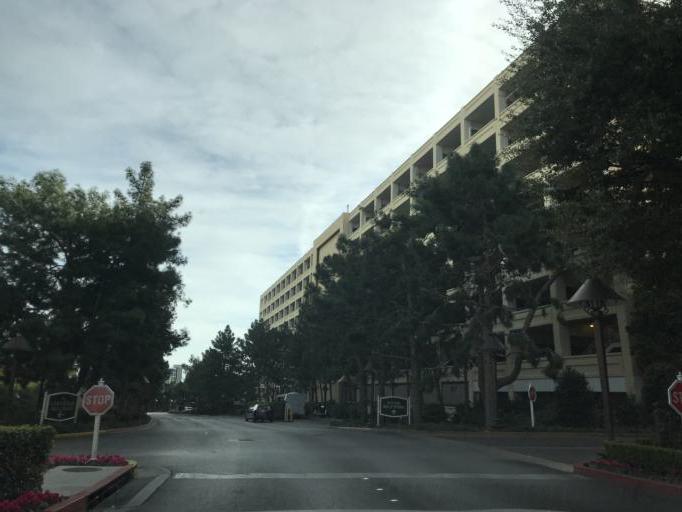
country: US
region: Nevada
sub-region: Clark County
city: Paradise
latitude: 36.1296
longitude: -115.1639
